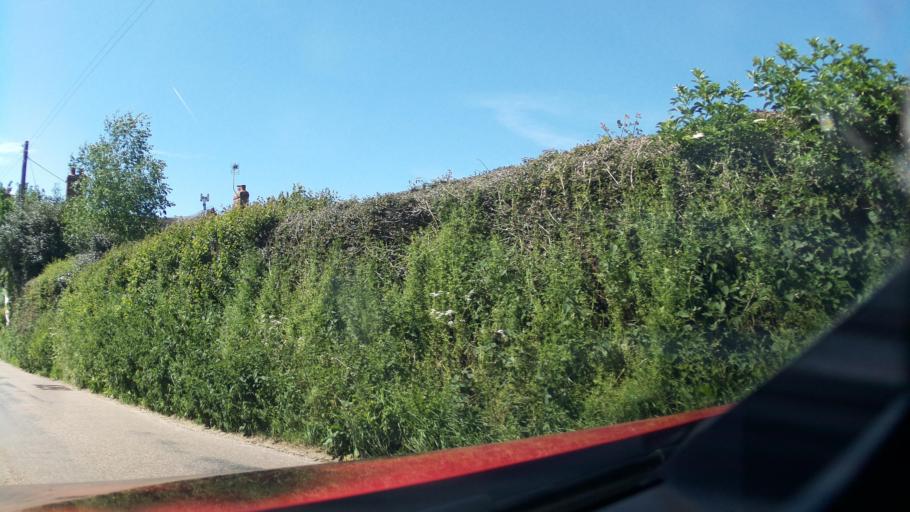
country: GB
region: England
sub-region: Devon
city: Ottery St Mary
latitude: 50.7382
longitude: -3.2740
